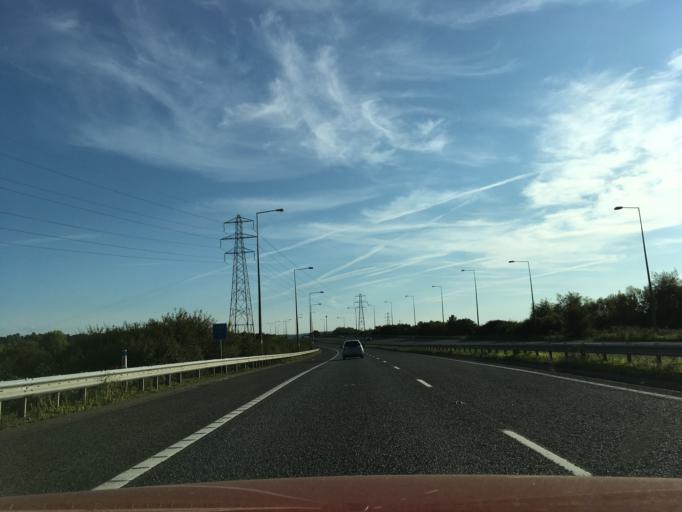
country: GB
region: England
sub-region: South Gloucestershire
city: Severn Beach
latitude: 51.5110
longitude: -2.6649
